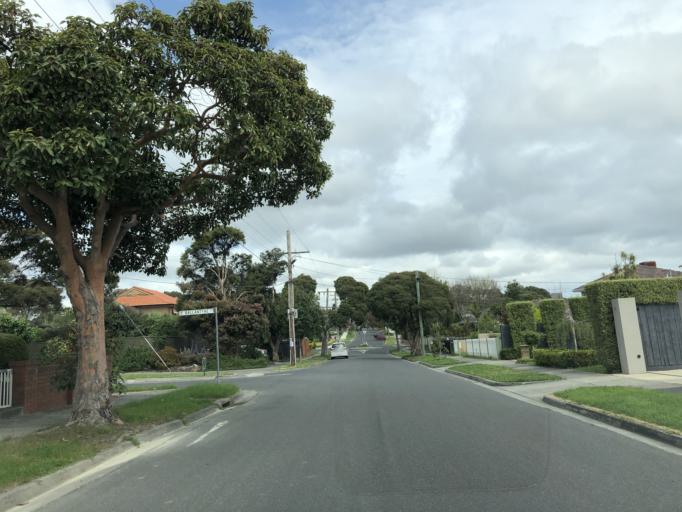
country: AU
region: Victoria
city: Burwood East
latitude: -37.8498
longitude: 145.1584
